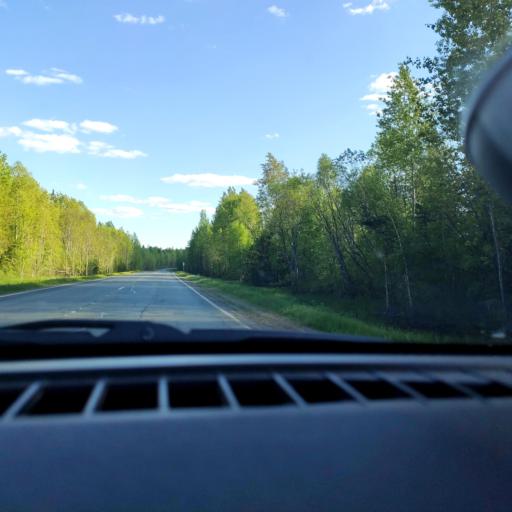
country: RU
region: Perm
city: Polazna
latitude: 58.2695
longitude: 56.1672
